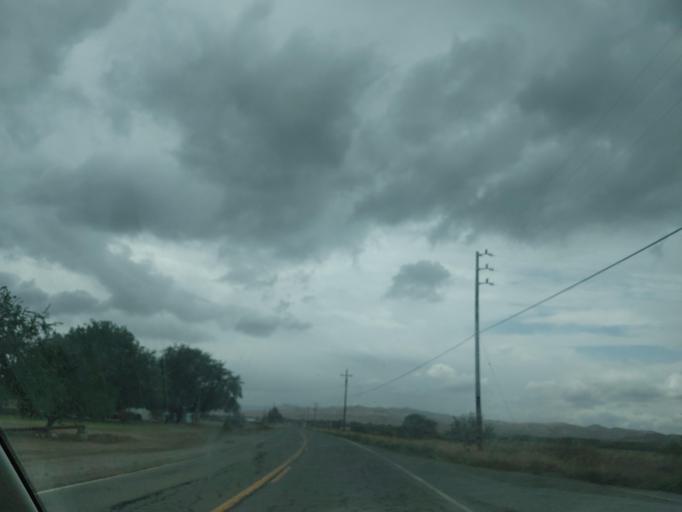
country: US
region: California
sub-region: Stanislaus County
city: Newman
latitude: 37.3338
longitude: -121.0874
